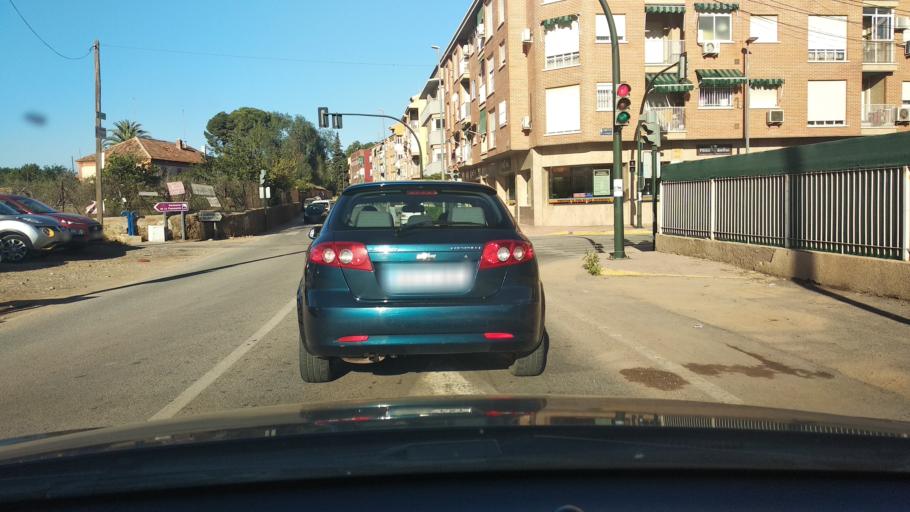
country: ES
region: Murcia
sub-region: Murcia
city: Murcia
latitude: 37.9445
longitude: -1.1233
